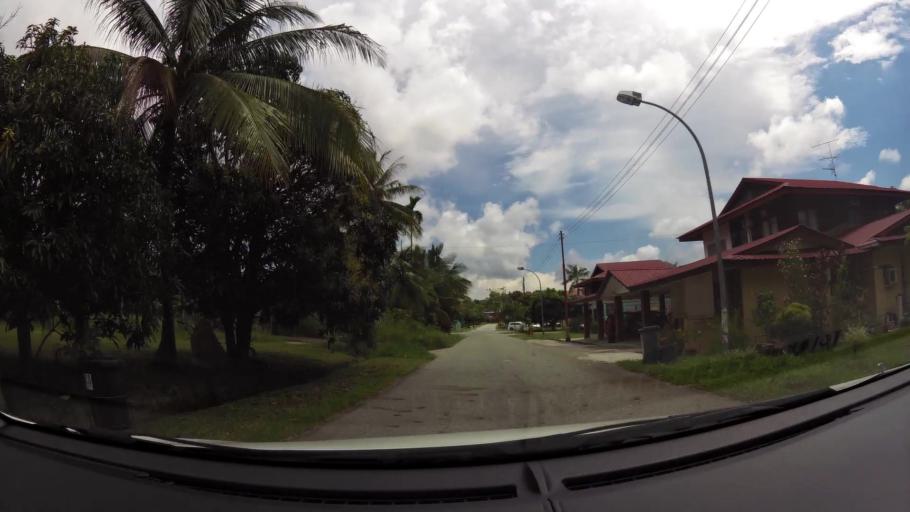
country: BN
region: Brunei and Muara
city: Bandar Seri Begawan
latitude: 4.9882
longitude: 114.9455
